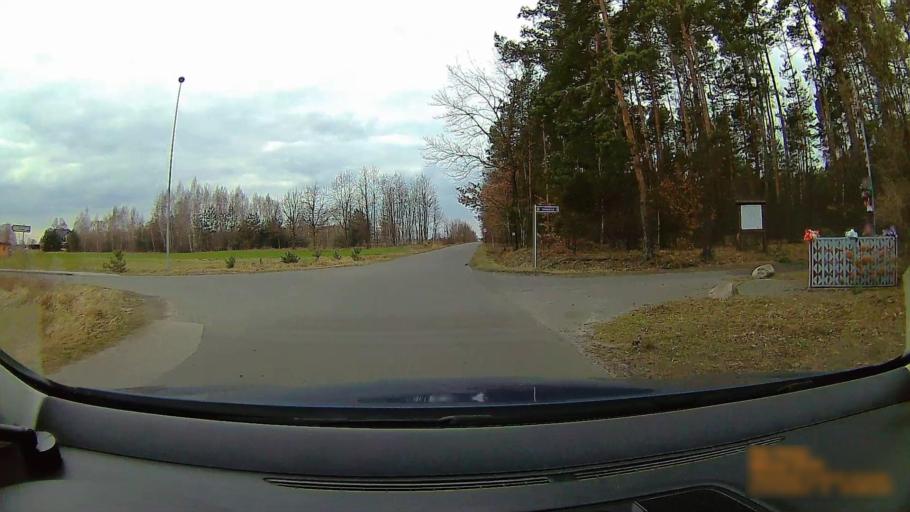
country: PL
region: Greater Poland Voivodeship
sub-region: Powiat koninski
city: Rychwal
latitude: 52.0803
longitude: 18.1343
